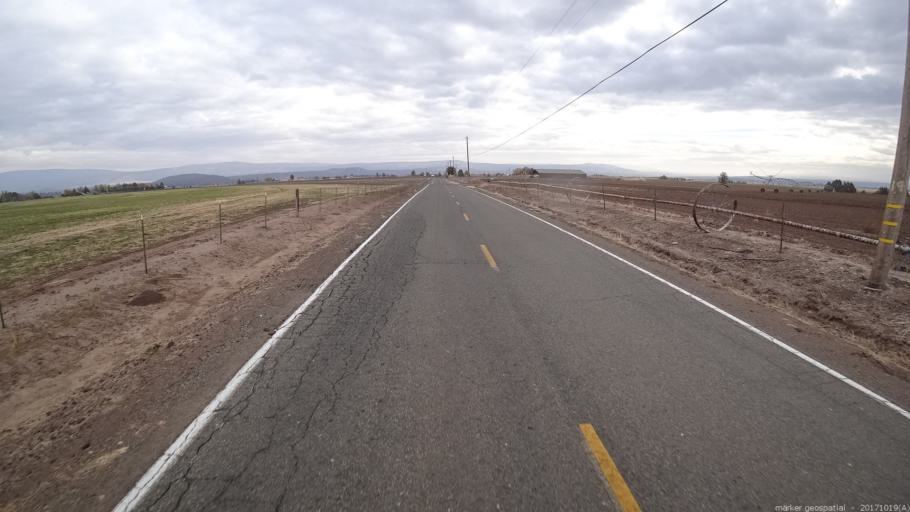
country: US
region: California
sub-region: Shasta County
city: Burney
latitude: 41.0333
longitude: -121.3692
